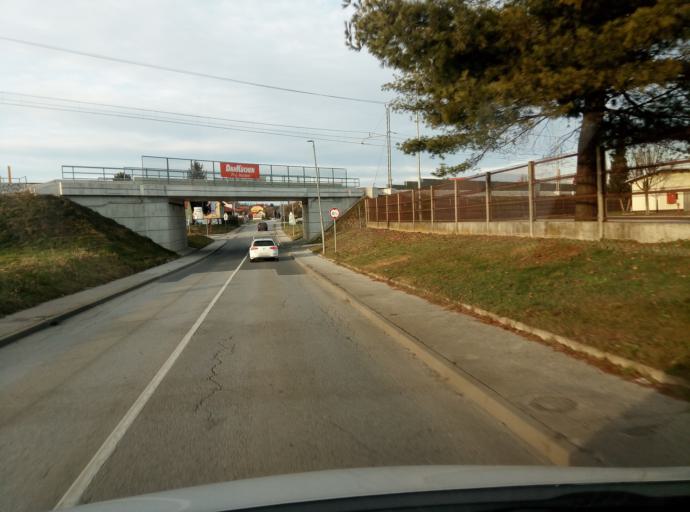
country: SI
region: Ptuj
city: Ptuj
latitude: 46.4105
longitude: 15.8655
